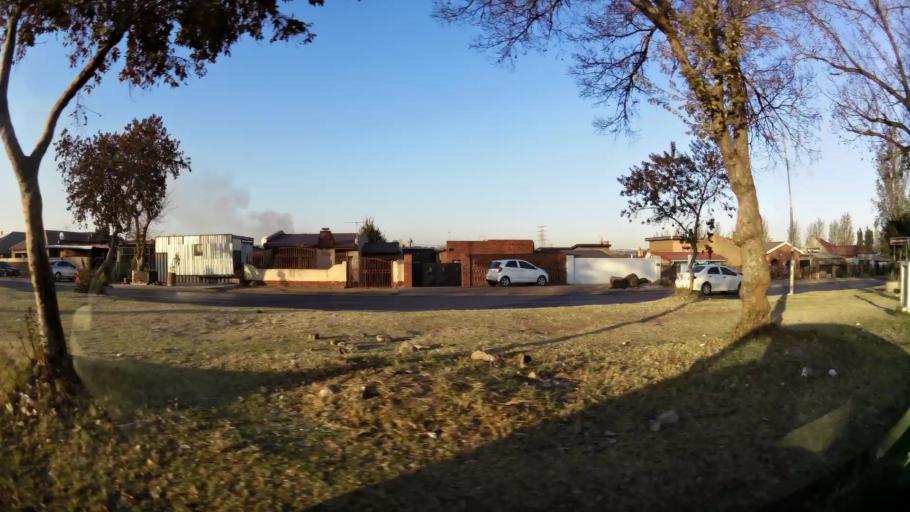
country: ZA
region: Gauteng
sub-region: City of Johannesburg Metropolitan Municipality
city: Soweto
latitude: -26.2438
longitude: 27.8813
